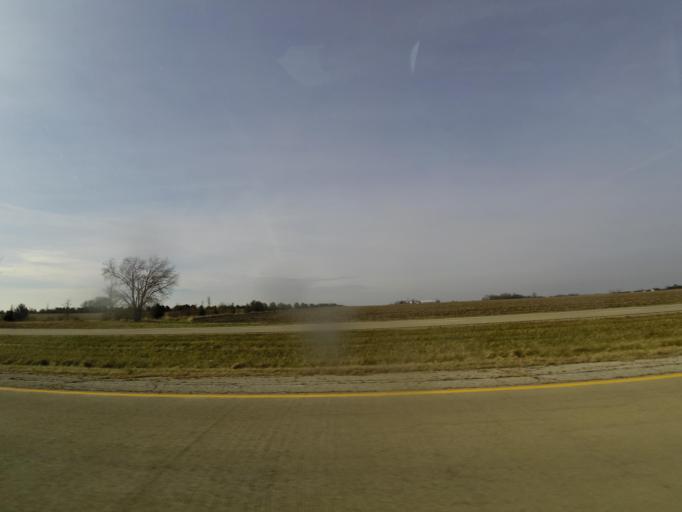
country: US
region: Illinois
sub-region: McLean County
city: Heyworth
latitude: 40.3892
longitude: -88.9894
